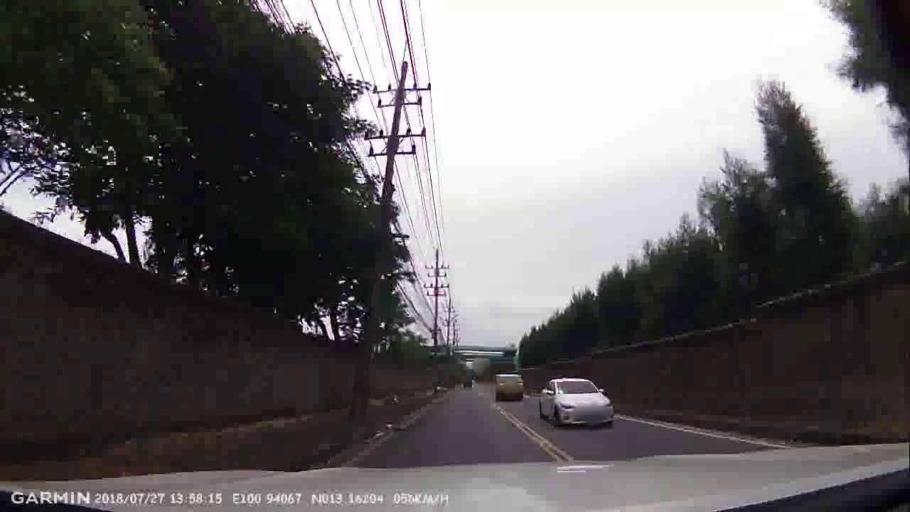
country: TH
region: Chon Buri
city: Si Racha
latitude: 13.1621
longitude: 100.9406
